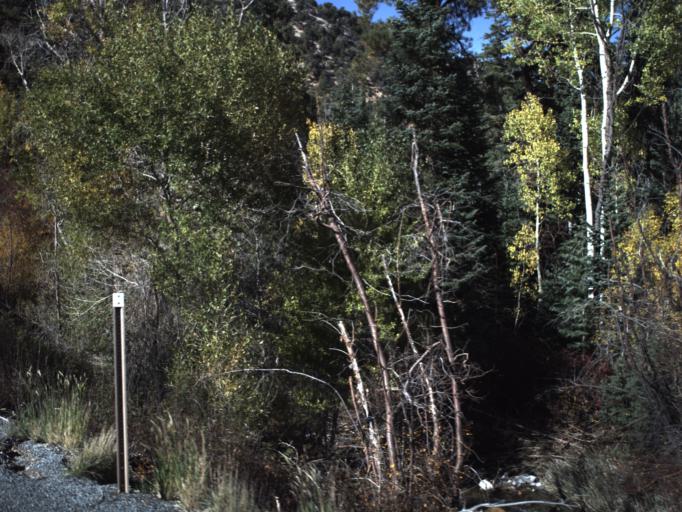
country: US
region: Utah
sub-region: Iron County
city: Parowan
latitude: 37.7619
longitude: -112.8503
